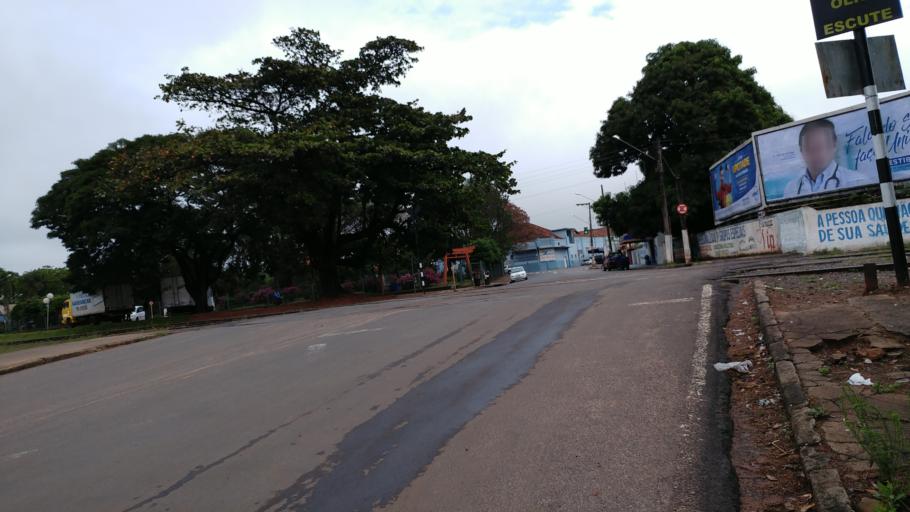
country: BR
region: Sao Paulo
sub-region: Paraguacu Paulista
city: Paraguacu Paulista
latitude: -22.4125
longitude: -50.5719
